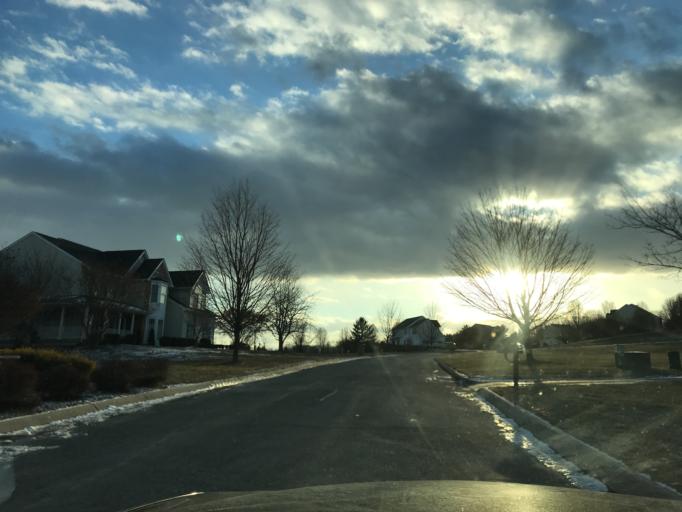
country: US
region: Maryland
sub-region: Harford County
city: Bel Air North
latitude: 39.5861
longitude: -76.3778
